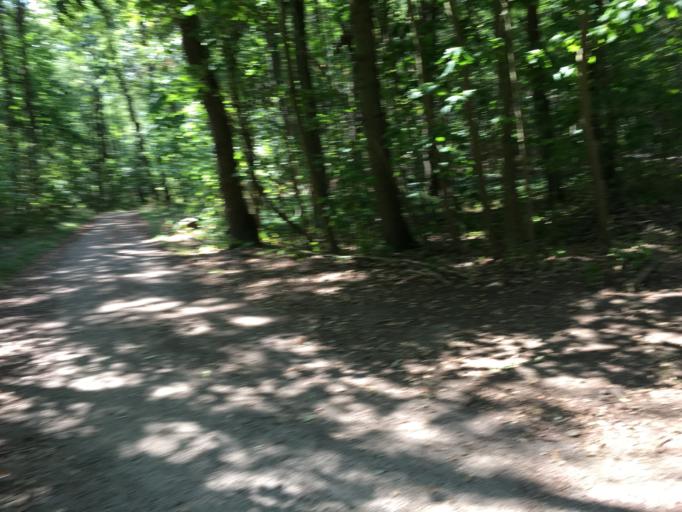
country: DE
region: North Rhine-Westphalia
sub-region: Regierungsbezirk Koln
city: Dueren
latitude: 50.7752
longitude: 6.5078
